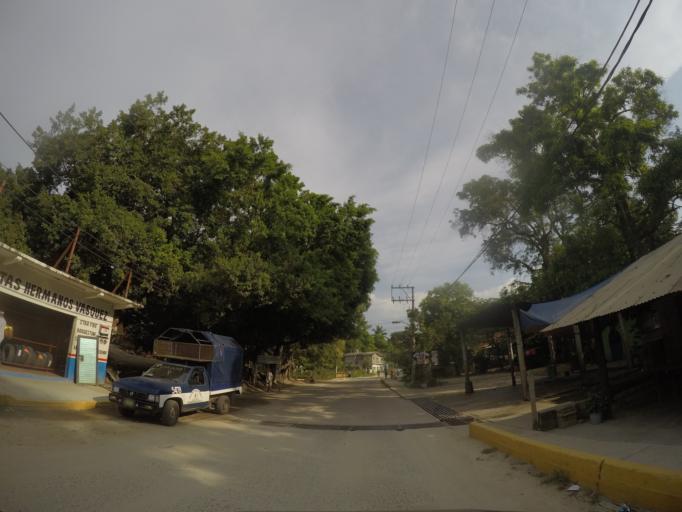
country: MX
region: Oaxaca
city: San Pedro Pochutla
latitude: 15.7526
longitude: -96.4646
